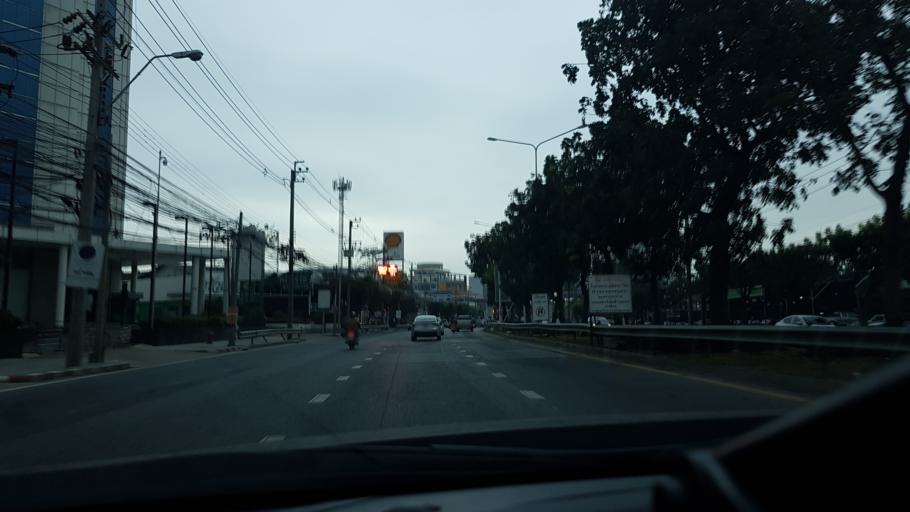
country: TH
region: Bangkok
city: Chatuchak
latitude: 13.8240
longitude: 100.5732
